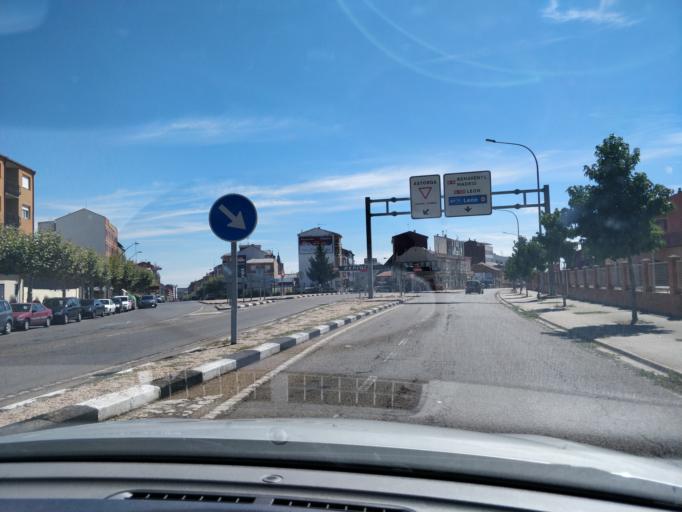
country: ES
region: Castille and Leon
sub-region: Provincia de Leon
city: Astorga
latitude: 42.4604
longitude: -6.0653
